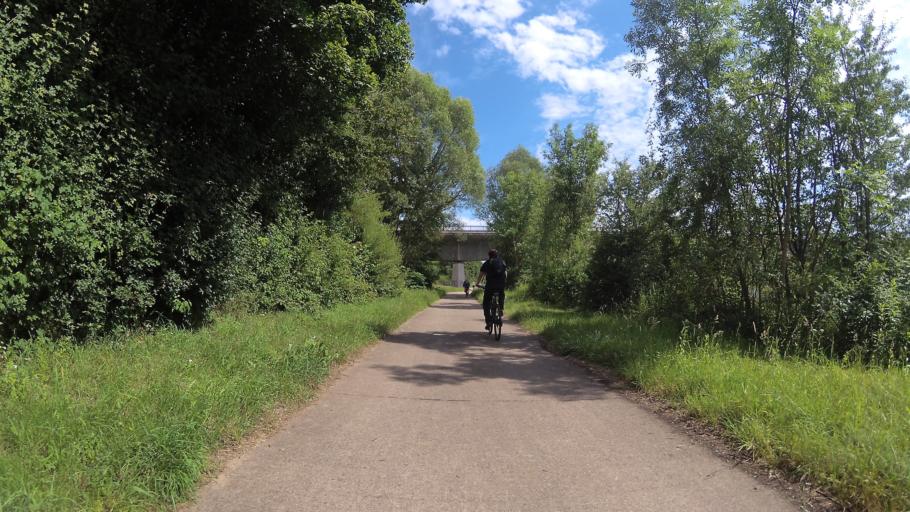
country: DE
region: Saarland
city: Merzig
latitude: 49.4643
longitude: 6.6135
